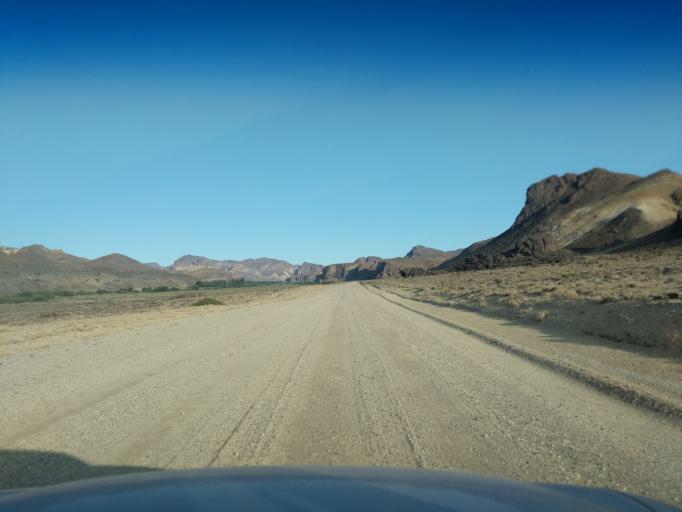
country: AR
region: Chubut
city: Leleque
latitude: -42.6380
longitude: -70.2141
